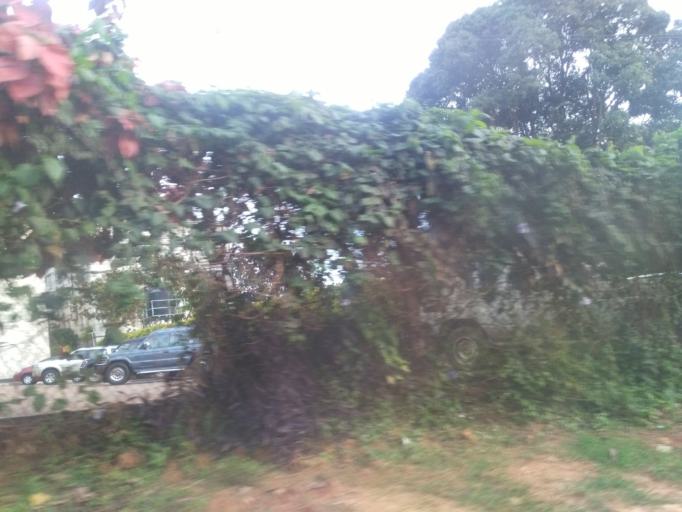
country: UG
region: Central Region
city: Kampala Central Division
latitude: 0.3404
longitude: 32.5776
